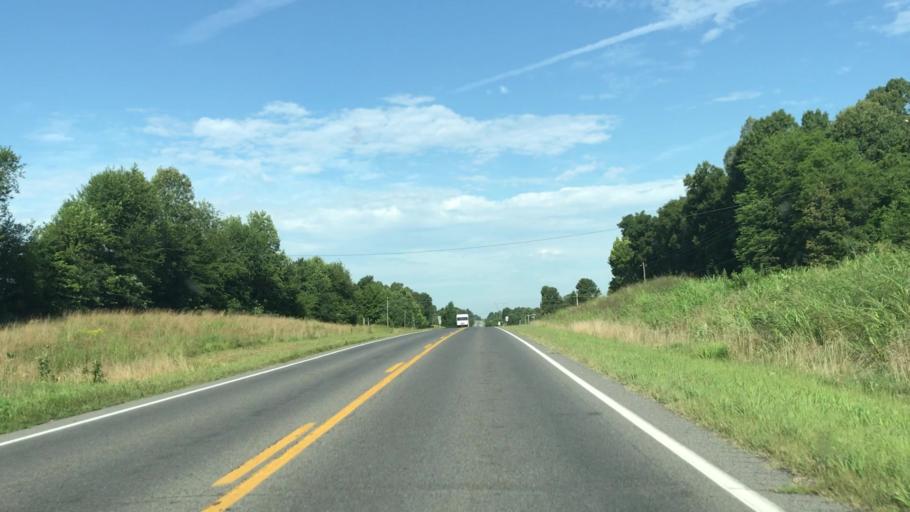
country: US
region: Kentucky
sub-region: Marshall County
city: Calvert City
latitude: 37.0052
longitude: -88.3991
